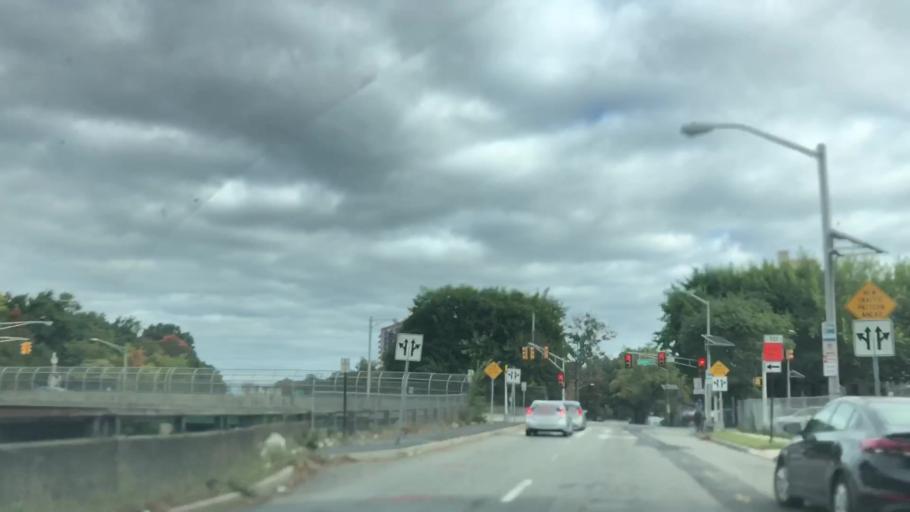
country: US
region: New Jersey
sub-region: Essex County
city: East Orange
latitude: 40.7657
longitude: -74.2044
